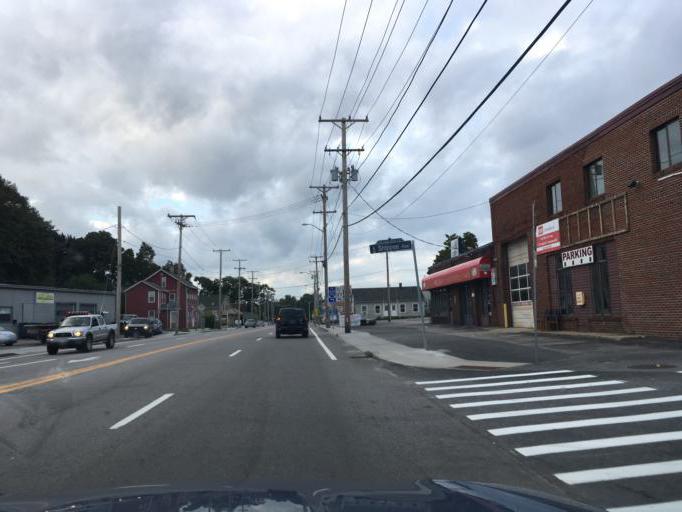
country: US
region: Rhode Island
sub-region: Kent County
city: Warwick
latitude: 41.7001
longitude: -71.4534
